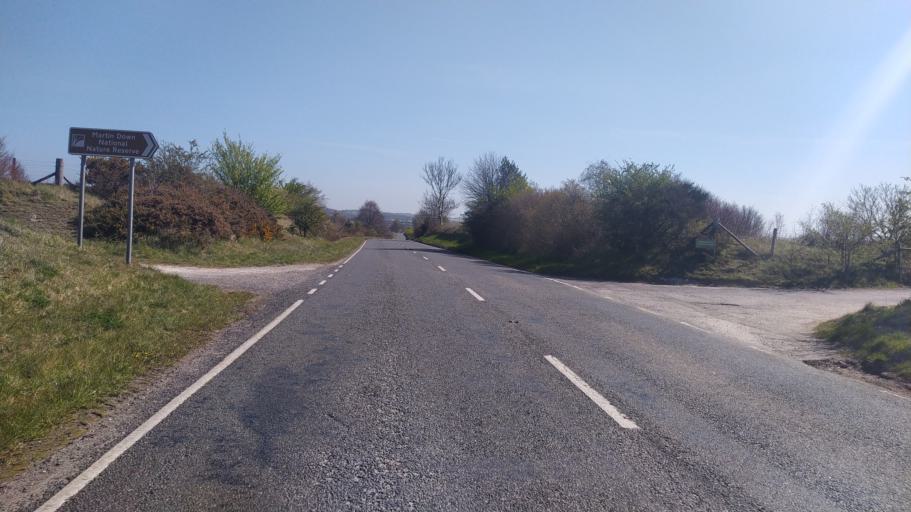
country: GB
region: England
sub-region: Wiltshire
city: Bower Chalke
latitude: 50.9806
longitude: -1.9491
